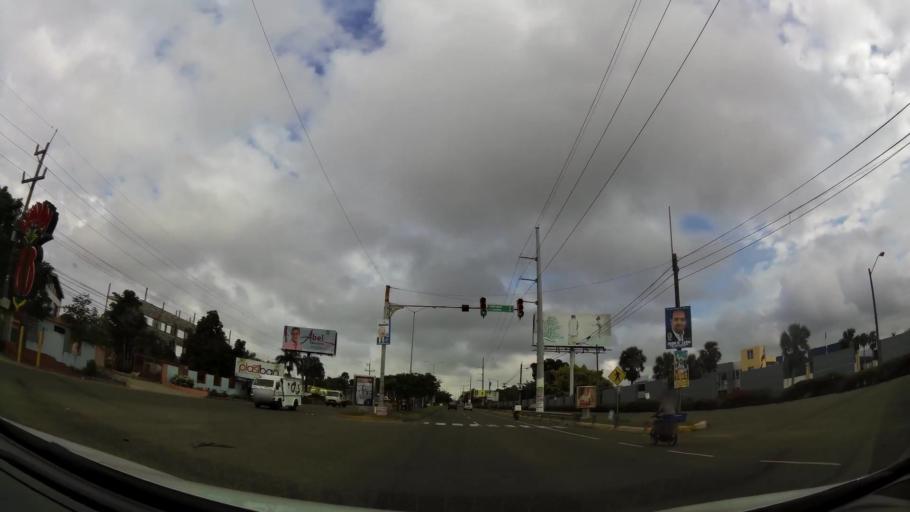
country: DO
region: Santiago
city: Licey al Medio
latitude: 19.4209
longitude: -70.6484
